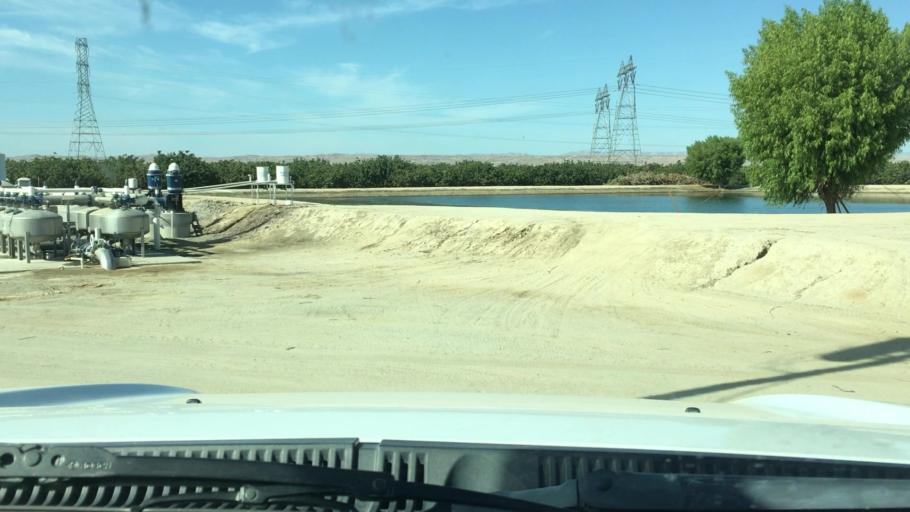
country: US
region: California
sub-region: Kern County
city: Buttonwillow
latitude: 35.3731
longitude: -119.3858
